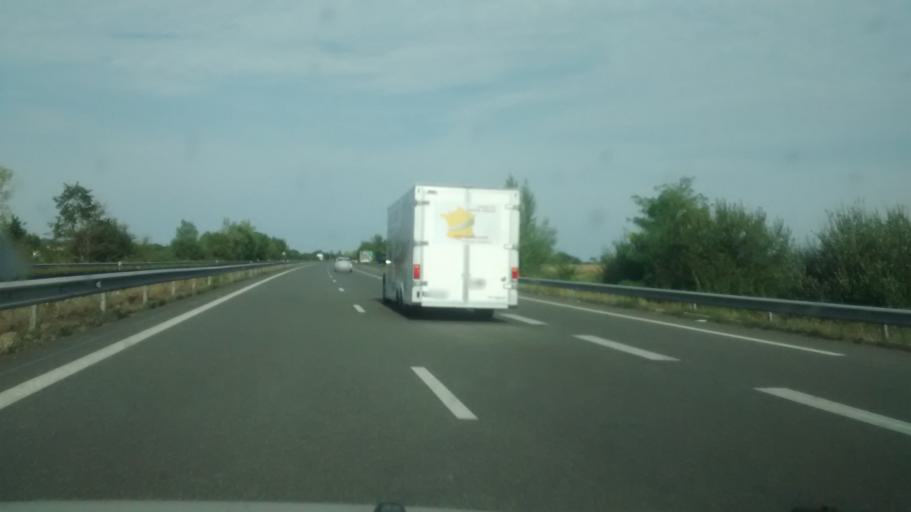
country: FR
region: Midi-Pyrenees
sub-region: Departement du Tarn-et-Garonne
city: Saint-Nicolas-de-la-Grave
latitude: 44.0448
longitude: 0.9952
